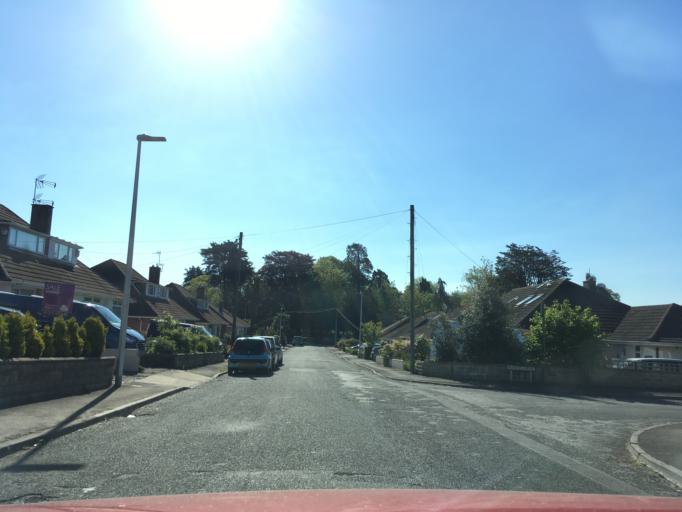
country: GB
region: England
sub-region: North Somerset
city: Portishead
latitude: 51.4736
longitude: -2.7756
